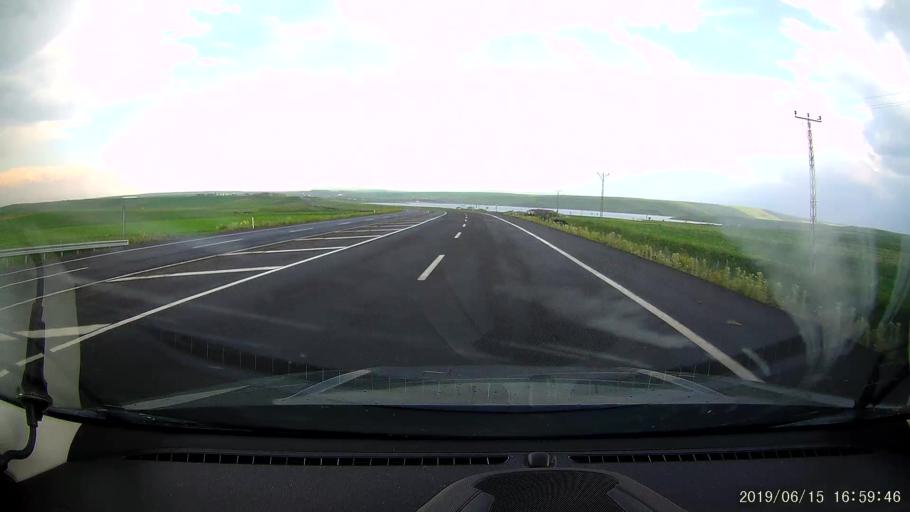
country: TR
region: Kars
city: Susuz
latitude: 40.7472
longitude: 43.1528
